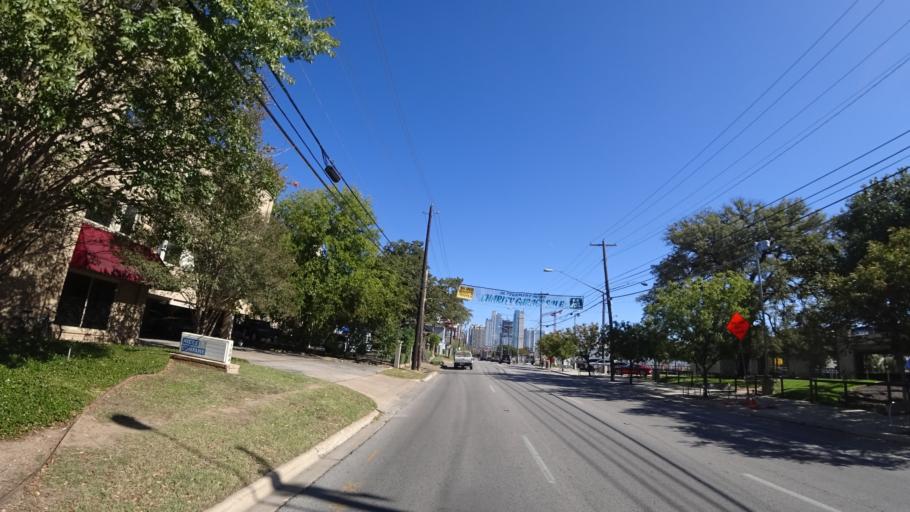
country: US
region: Texas
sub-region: Travis County
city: Austin
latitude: 30.2734
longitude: -97.7625
